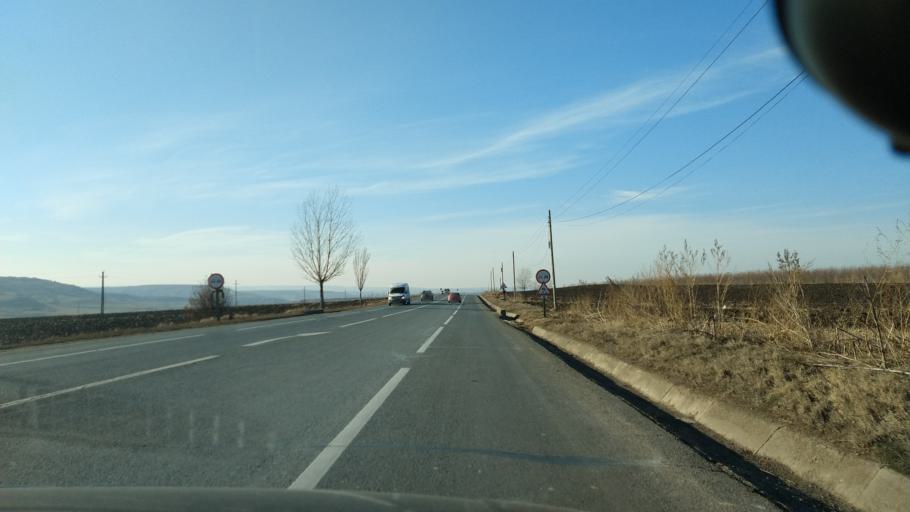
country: RO
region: Iasi
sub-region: Comuna Baltati
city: Baltati
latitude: 47.2189
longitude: 27.1118
